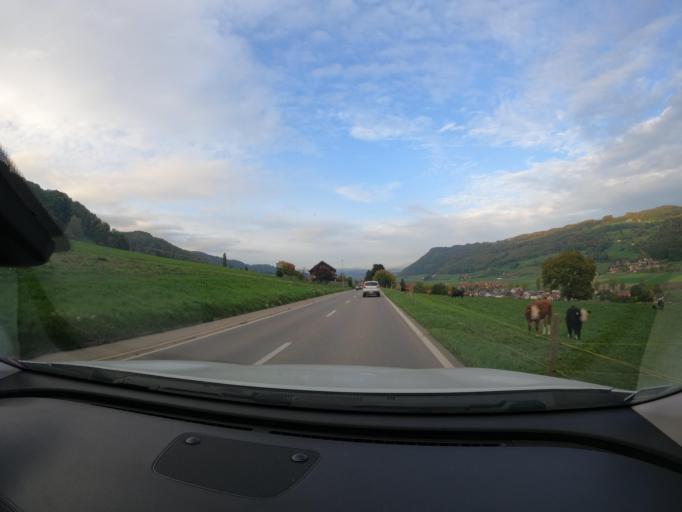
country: CH
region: Bern
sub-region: Bern-Mittelland District
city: Toffen
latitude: 46.8523
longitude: 7.4905
